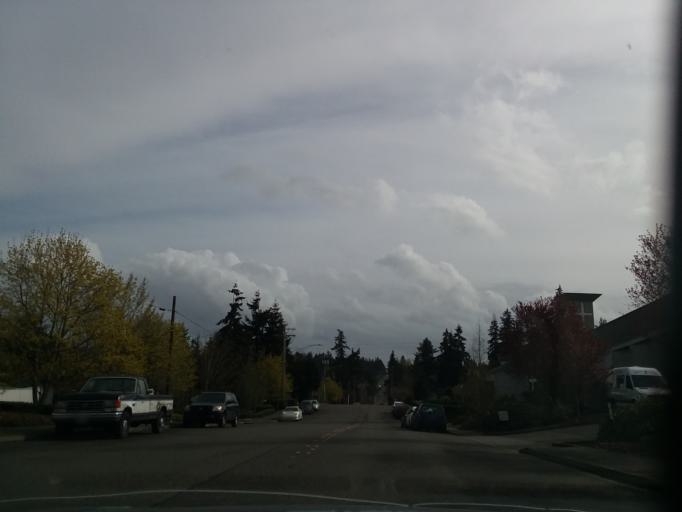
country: US
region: Washington
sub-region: Snohomish County
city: Lynnwood
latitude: 47.8086
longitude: -122.3220
